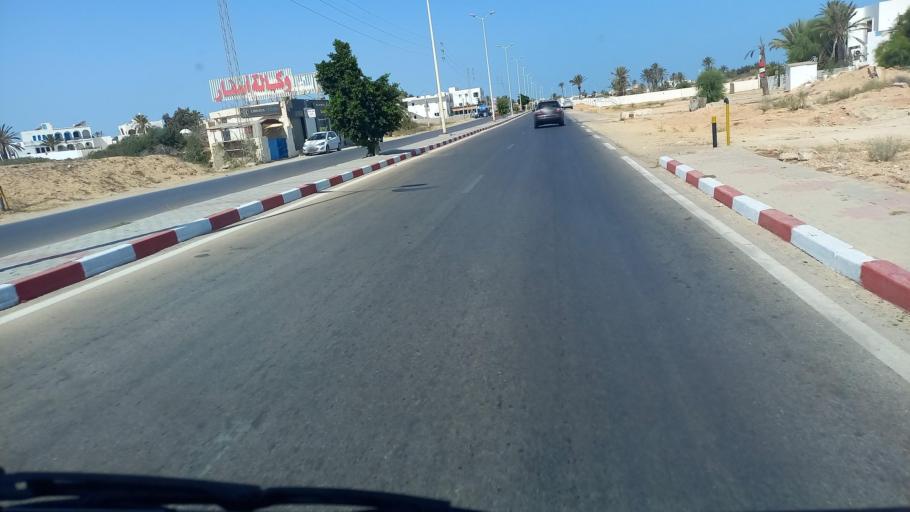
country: TN
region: Madanin
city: Midoun
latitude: 33.8609
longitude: 10.9690
